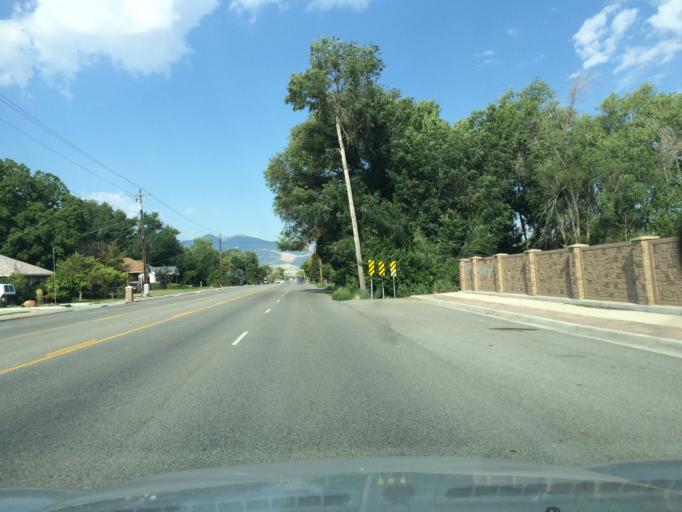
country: US
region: Utah
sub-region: Salt Lake County
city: West Valley City
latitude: 40.6966
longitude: -112.0177
